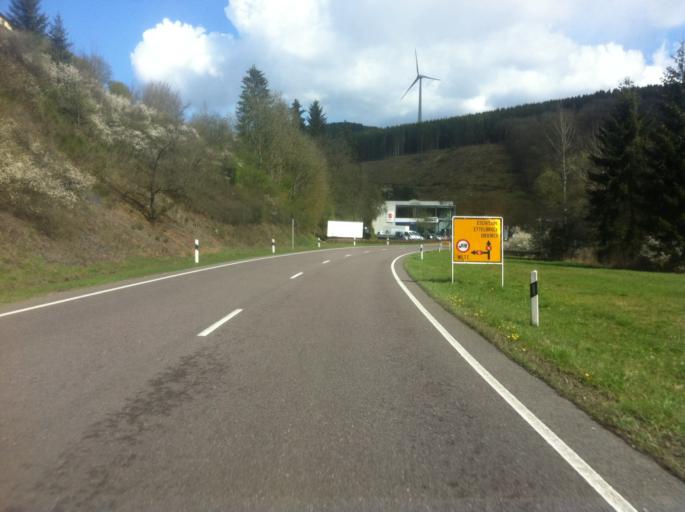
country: LU
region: Diekirch
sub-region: Canton de Wiltz
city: Esch-sur-Sure
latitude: 49.9331
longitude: 5.9374
